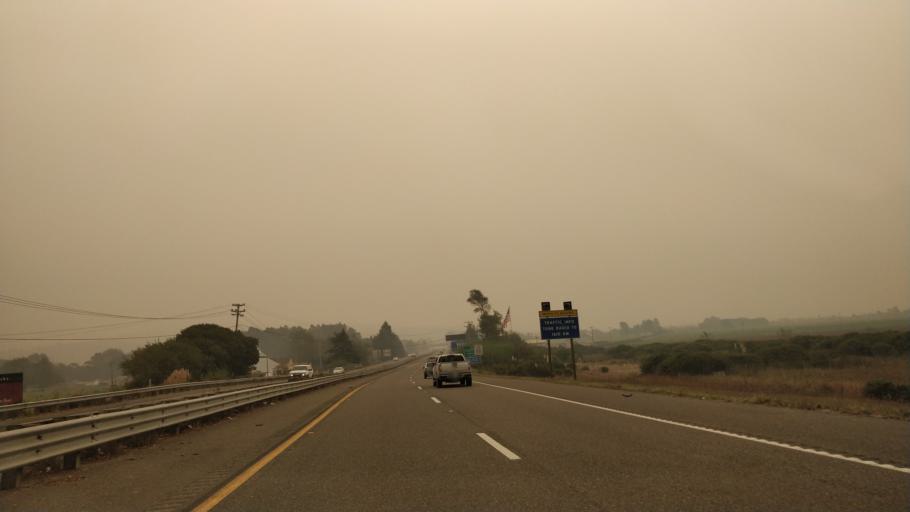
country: US
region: California
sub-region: Humboldt County
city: McKinleyville
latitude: 40.9149
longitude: -124.0920
